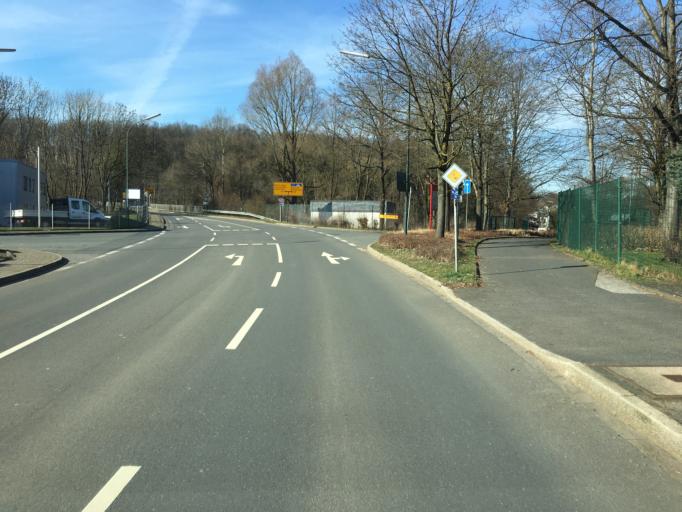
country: DE
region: North Rhine-Westphalia
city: Huckeswagen
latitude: 51.1398
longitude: 7.3523
